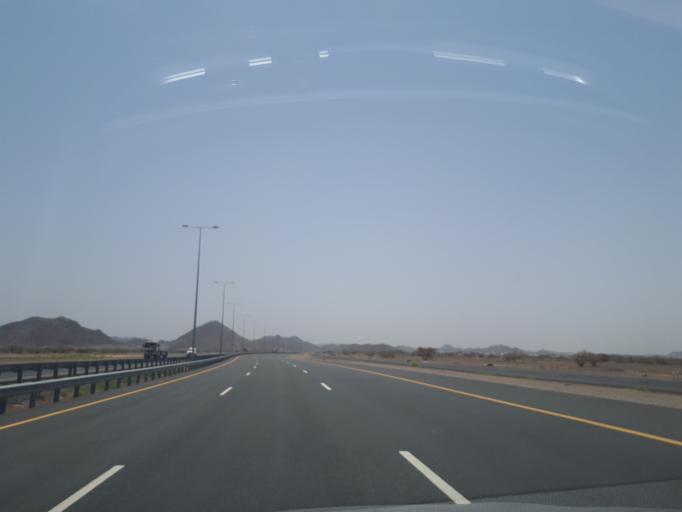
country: OM
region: Ash Sharqiyah
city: Ibra'
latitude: 22.7596
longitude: 58.5231
